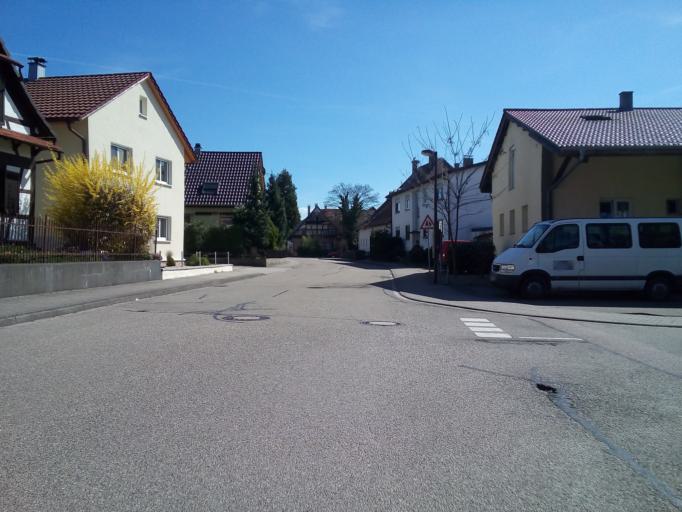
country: DE
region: Baden-Wuerttemberg
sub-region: Freiburg Region
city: Rheinau
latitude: 48.6515
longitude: 7.9277
